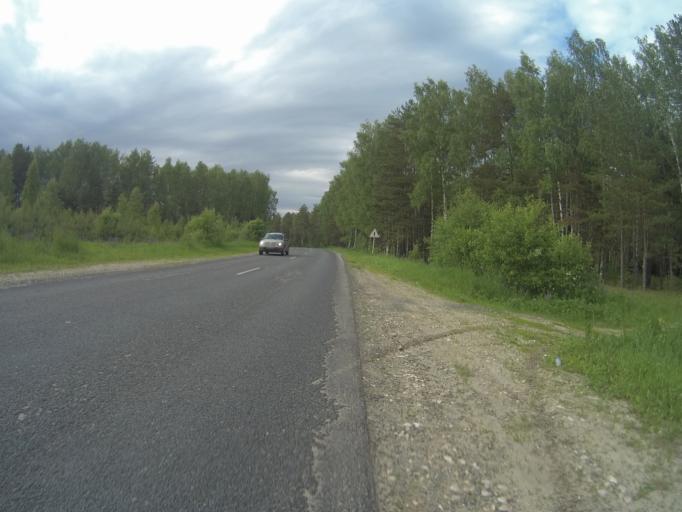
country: RU
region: Vladimir
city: Raduzhnyy
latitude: 55.9937
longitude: 40.2725
